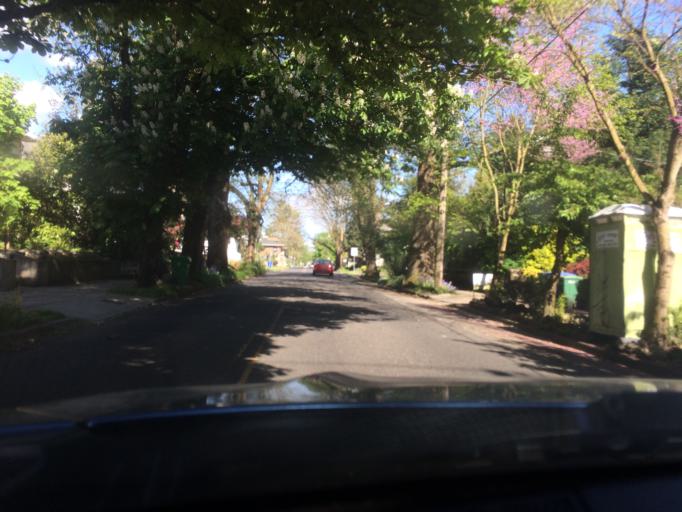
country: US
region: Oregon
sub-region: Multnomah County
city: Portland
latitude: 45.5555
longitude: -122.6575
